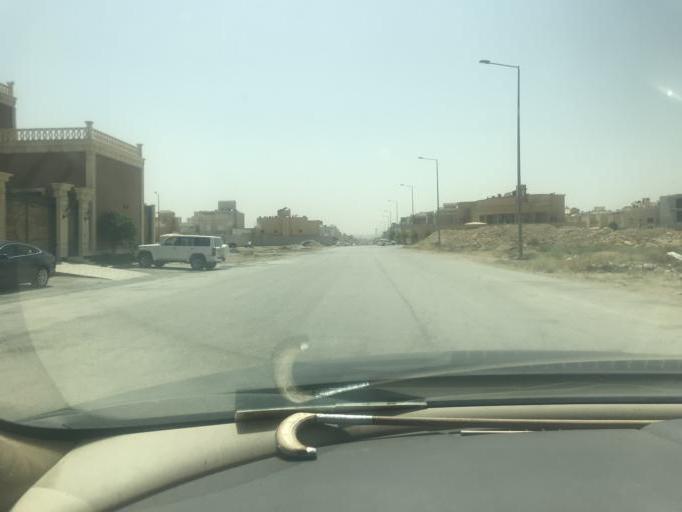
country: SA
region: Ar Riyad
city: Riyadh
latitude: 24.7861
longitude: 46.5860
